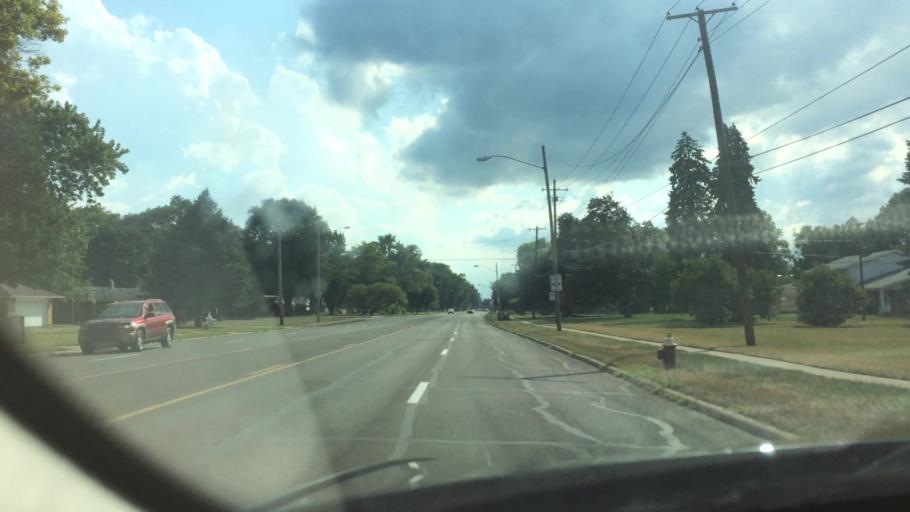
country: US
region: Ohio
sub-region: Wood County
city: Perrysburg
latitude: 41.6009
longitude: -83.6291
